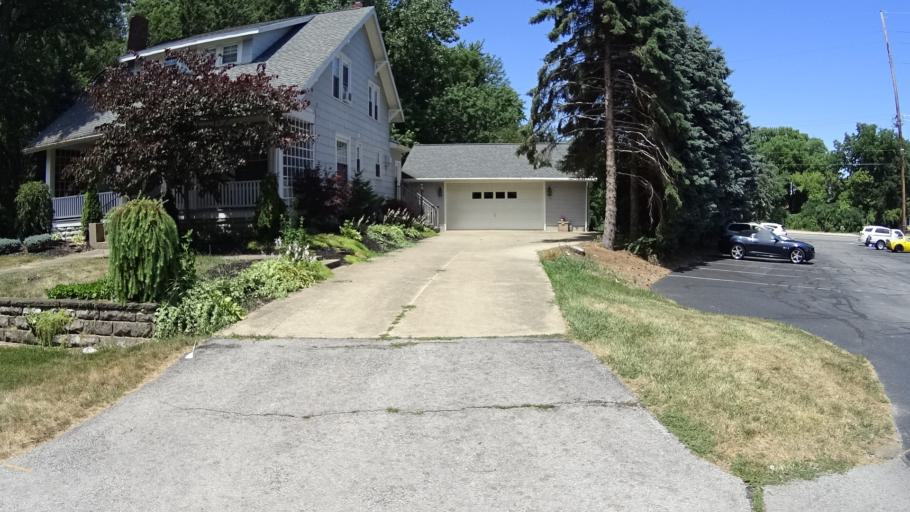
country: US
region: Ohio
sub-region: Erie County
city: Sandusky
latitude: 41.3951
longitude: -82.6526
